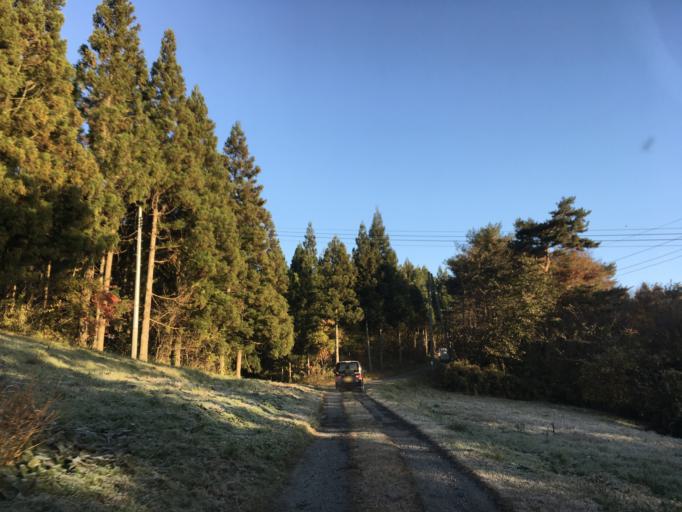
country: JP
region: Iwate
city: Ichinoseki
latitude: 38.7975
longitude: 141.1896
